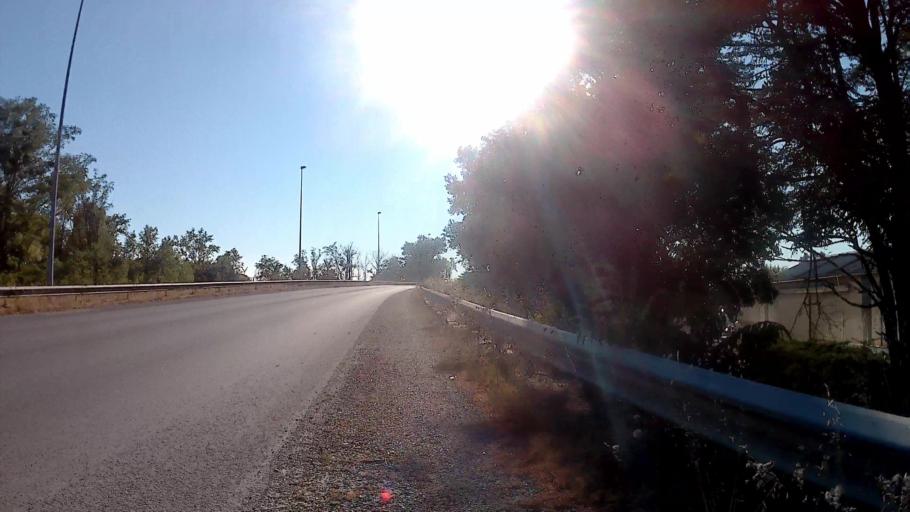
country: FR
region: Aquitaine
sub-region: Departement de la Gironde
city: Villenave-d'Ornon
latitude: 44.7821
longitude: -0.5415
